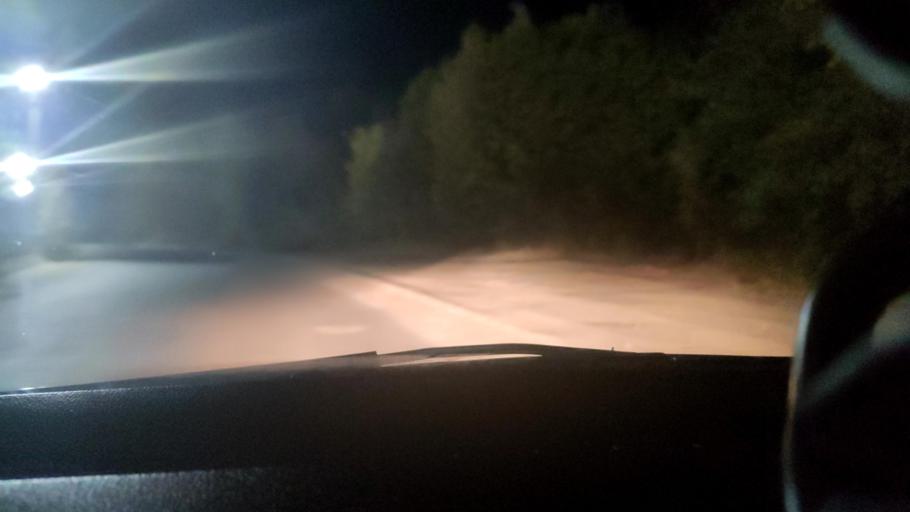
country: RU
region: Voronezj
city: Voronezh
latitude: 51.7281
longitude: 39.2120
